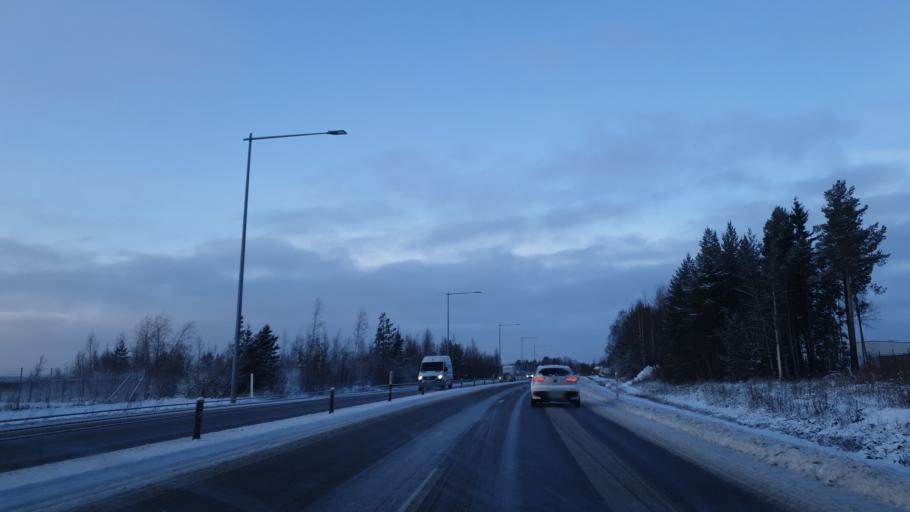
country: SE
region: Vaesterbotten
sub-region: Umea Kommun
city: Umea
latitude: 63.8004
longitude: 20.2739
